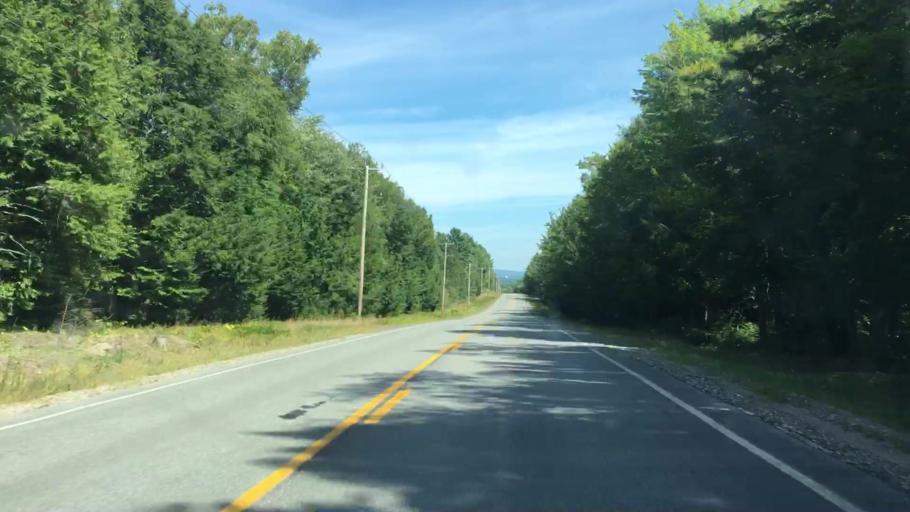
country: US
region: Maine
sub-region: Penobscot County
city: Howland
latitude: 45.2326
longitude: -68.7577
